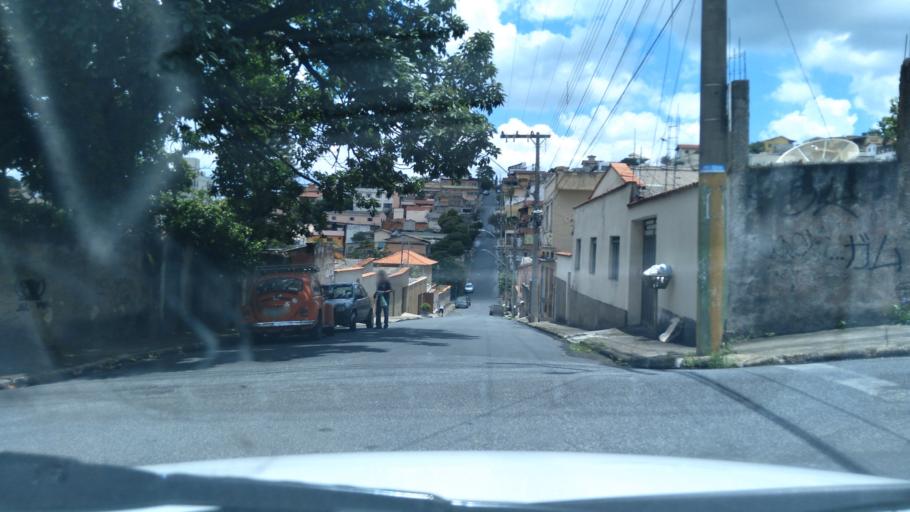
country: BR
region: Minas Gerais
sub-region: Belo Horizonte
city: Belo Horizonte
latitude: -19.9216
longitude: -43.9079
